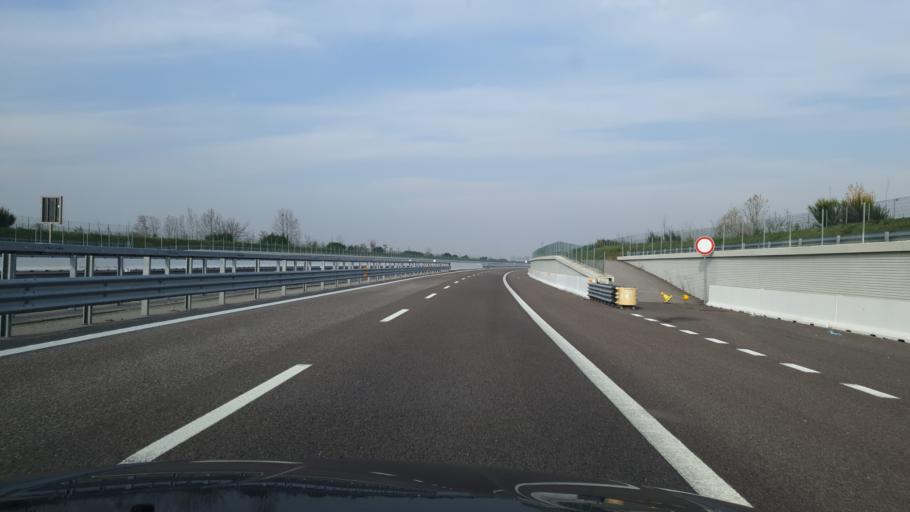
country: IT
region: Veneto
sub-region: Provincia di Vicenza
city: Agugliaro
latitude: 45.3186
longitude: 11.5754
